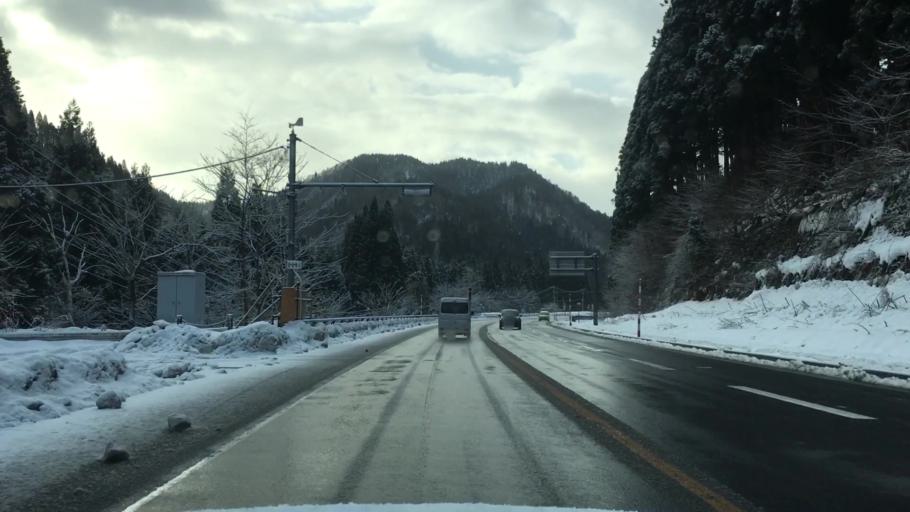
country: JP
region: Akita
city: Odate
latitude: 40.4113
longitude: 140.6120
